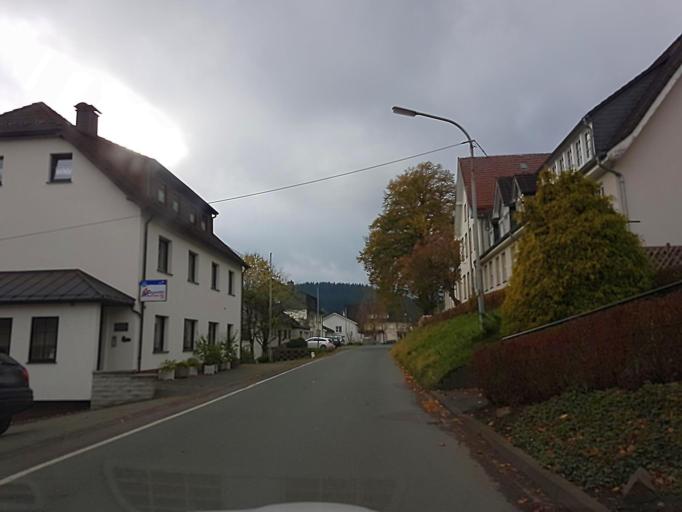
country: DE
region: North Rhine-Westphalia
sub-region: Regierungsbezirk Arnsberg
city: Drolshagen
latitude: 51.0657
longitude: 7.7820
